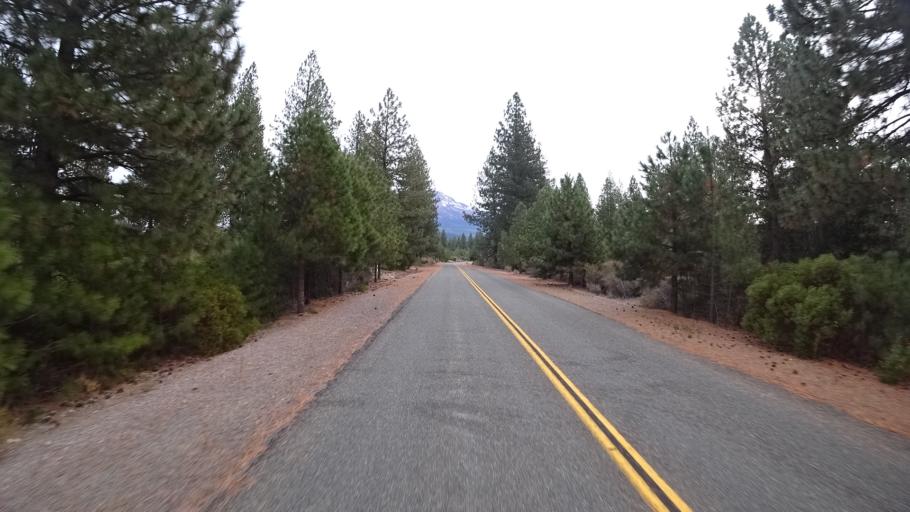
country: US
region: California
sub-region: Siskiyou County
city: Weed
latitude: 41.4131
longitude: -122.3681
